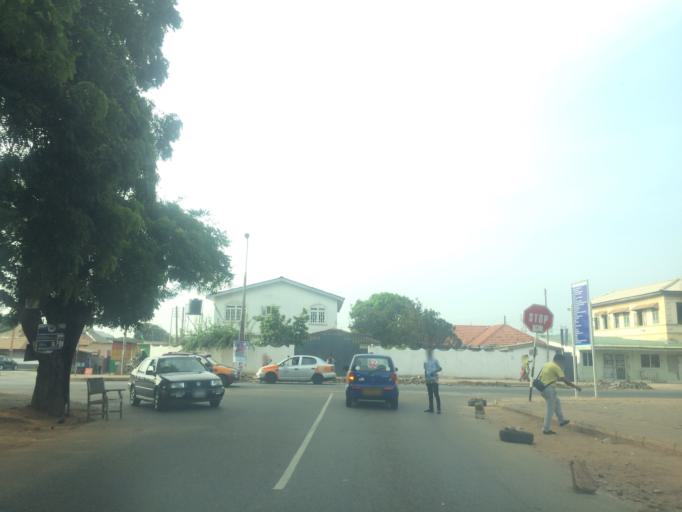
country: GH
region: Greater Accra
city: Accra
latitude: 5.5359
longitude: -0.2293
